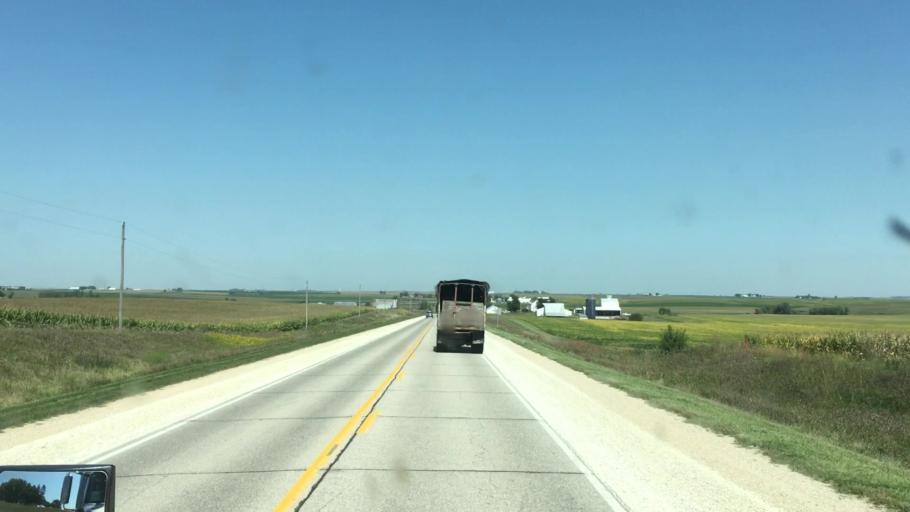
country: US
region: Iowa
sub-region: Tama County
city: Dysart
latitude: 42.0572
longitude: -92.2987
